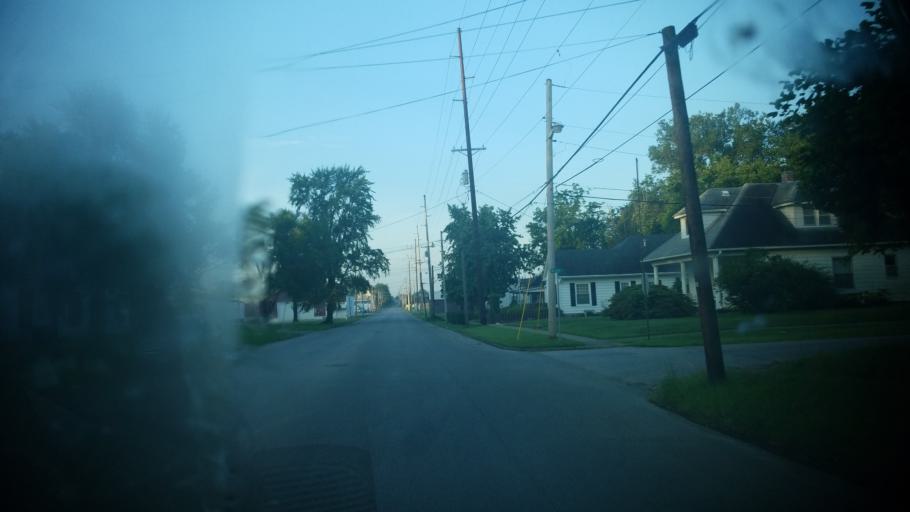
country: US
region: Illinois
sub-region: Wayne County
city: Fairfield
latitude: 38.3827
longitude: -88.3684
